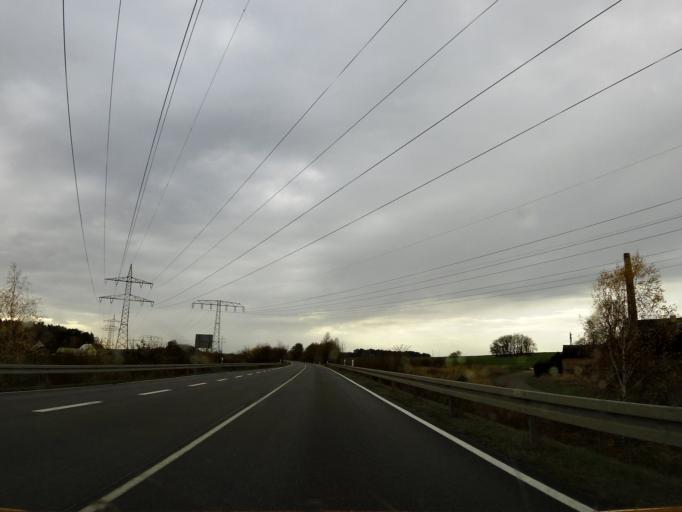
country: DE
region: Saxony-Anhalt
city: Gardelegen
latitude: 52.5339
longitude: 11.3700
